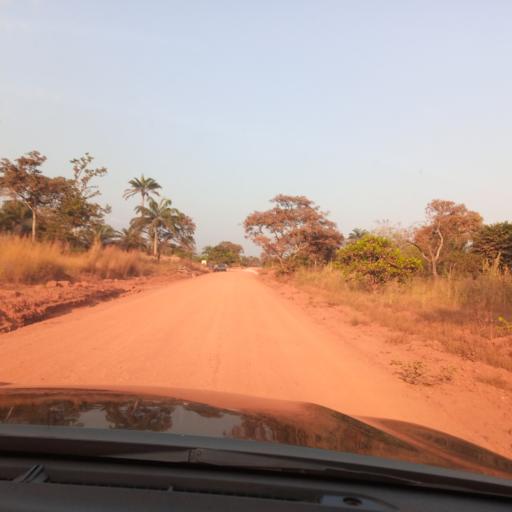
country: NG
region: Enugu
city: Aku
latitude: 6.7153
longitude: 7.3454
